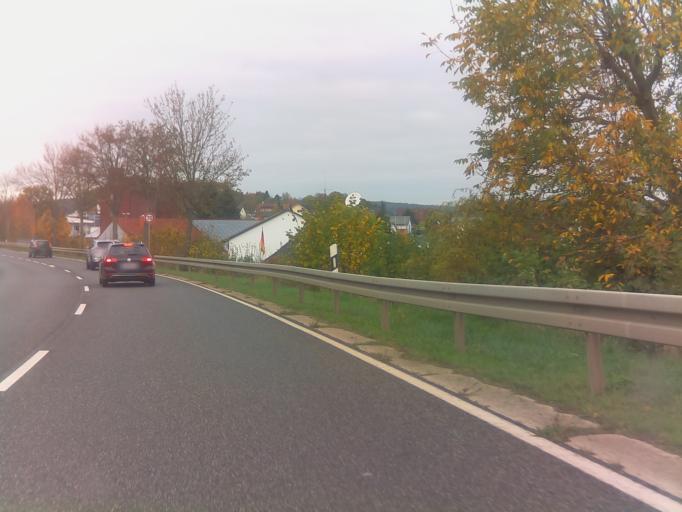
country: DE
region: Hesse
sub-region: Regierungsbezirk Darmstadt
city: Ranstadt
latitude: 50.3524
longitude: 8.9844
